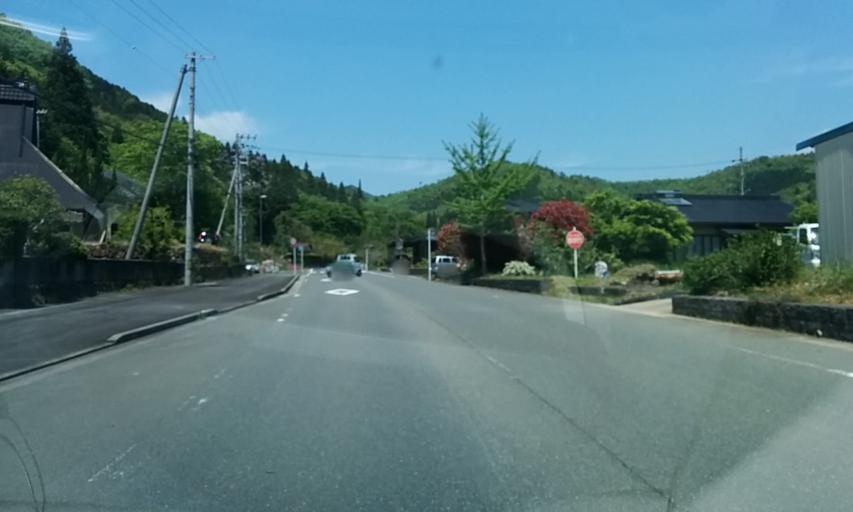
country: JP
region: Kyoto
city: Ayabe
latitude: 35.2449
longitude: 135.2657
